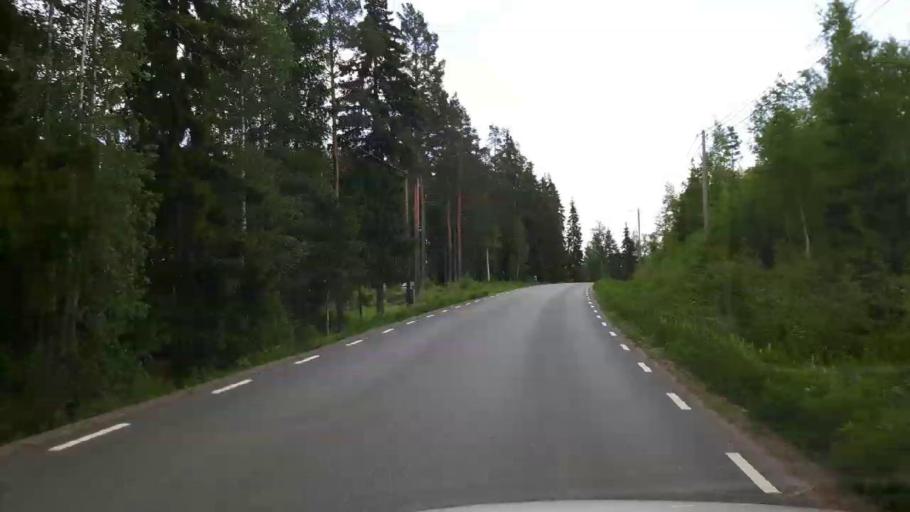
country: SE
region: Dalarna
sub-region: Faluns Kommun
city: Falun
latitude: 60.6640
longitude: 15.7588
